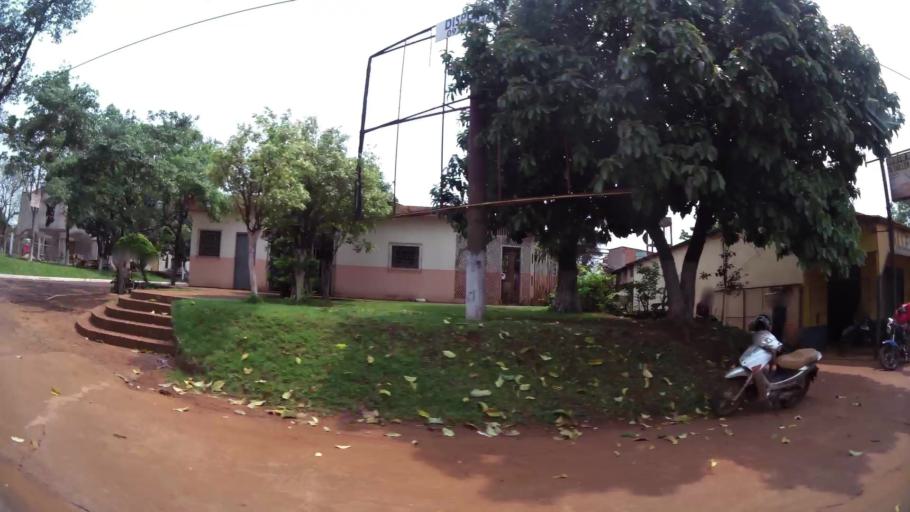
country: PY
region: Alto Parana
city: Presidente Franco
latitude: -25.5527
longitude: -54.6394
